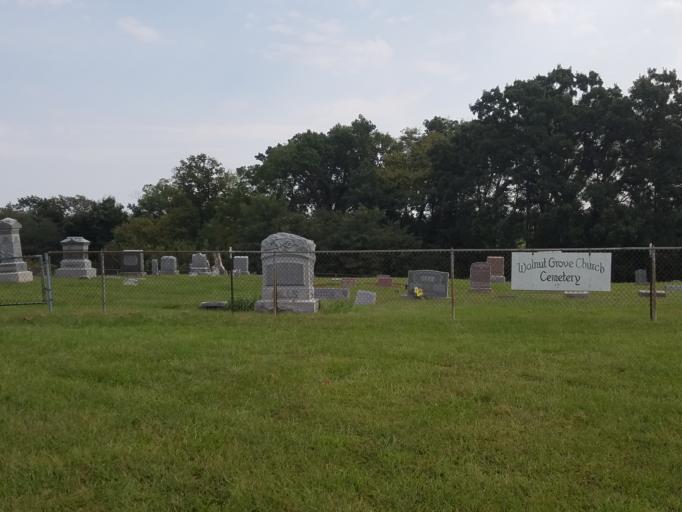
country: US
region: Missouri
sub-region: Cooper County
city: Boonville
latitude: 38.8715
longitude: -92.6427
